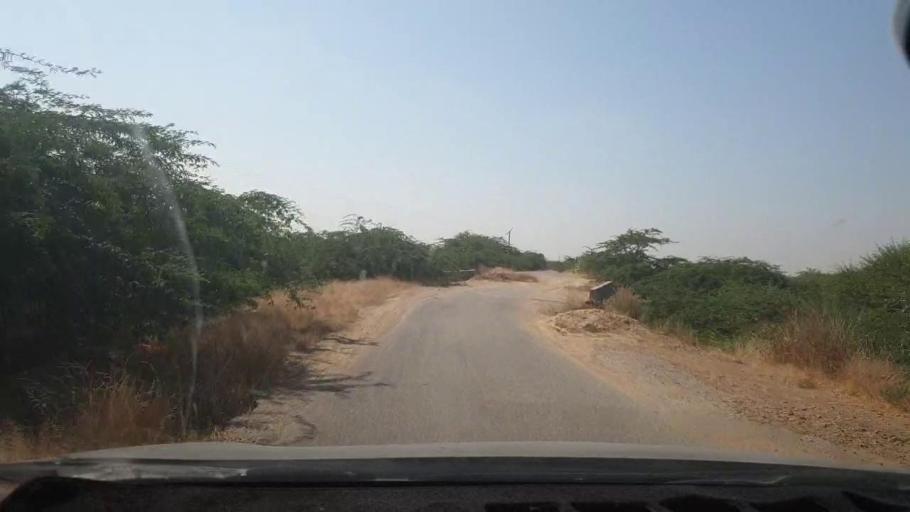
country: PK
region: Sindh
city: Malir Cantonment
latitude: 25.1556
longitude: 67.1379
